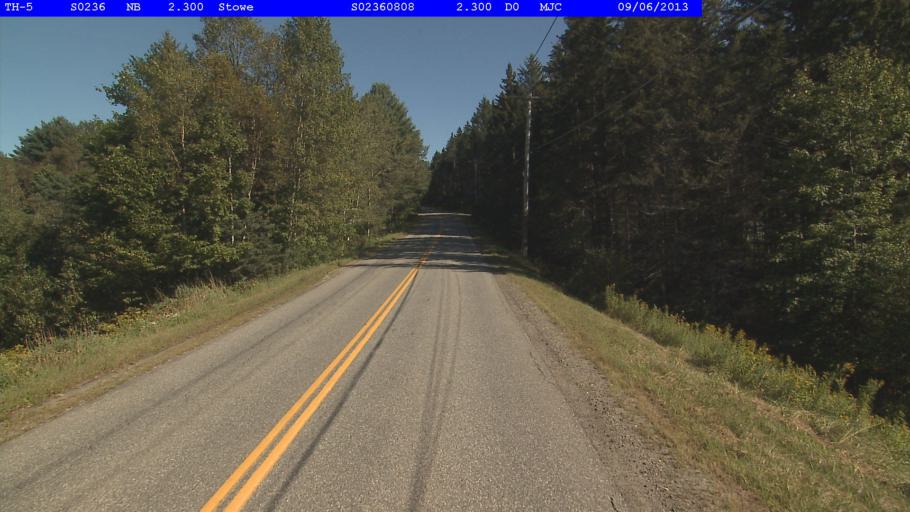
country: US
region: Vermont
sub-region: Washington County
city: Waterbury
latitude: 44.4580
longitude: -72.7291
